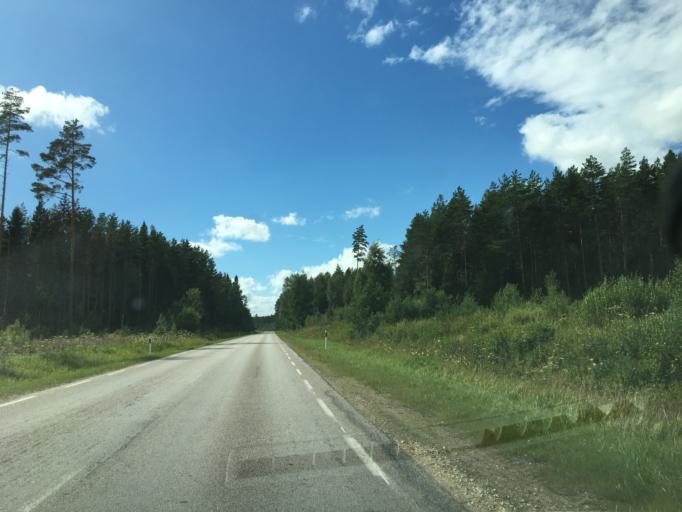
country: EE
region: Paernumaa
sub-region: Vaendra vald (alev)
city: Vandra
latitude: 58.5787
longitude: 25.2440
